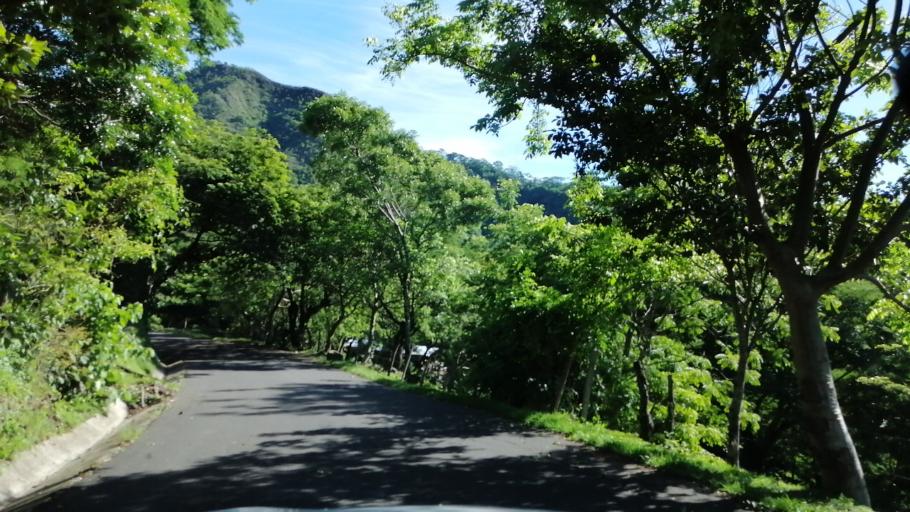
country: SV
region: Morazan
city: Corinto
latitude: 13.7919
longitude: -88.0121
